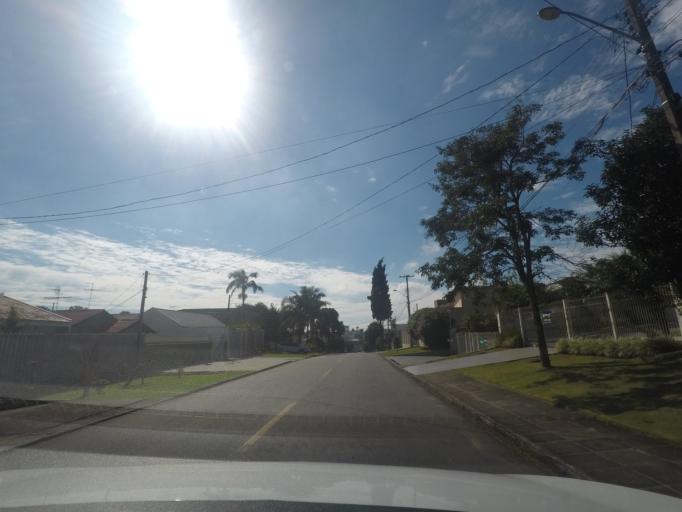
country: BR
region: Parana
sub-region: Sao Jose Dos Pinhais
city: Sao Jose dos Pinhais
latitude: -25.5087
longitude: -49.2629
